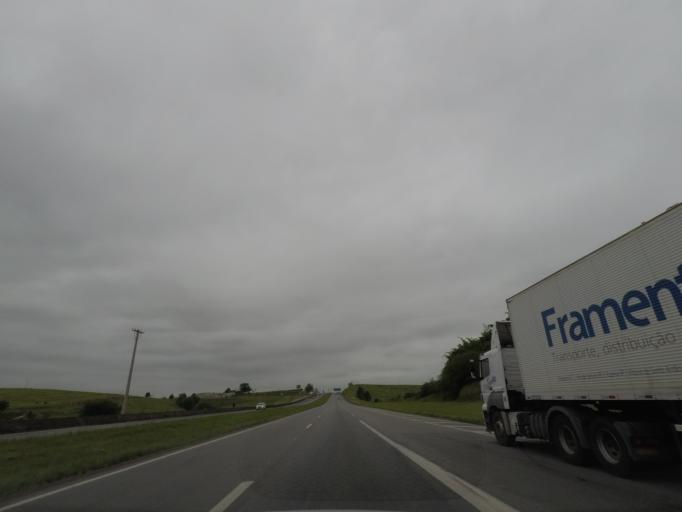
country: BR
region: Sao Paulo
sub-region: Jacarei
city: Jacarei
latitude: -23.2734
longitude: -46.0563
